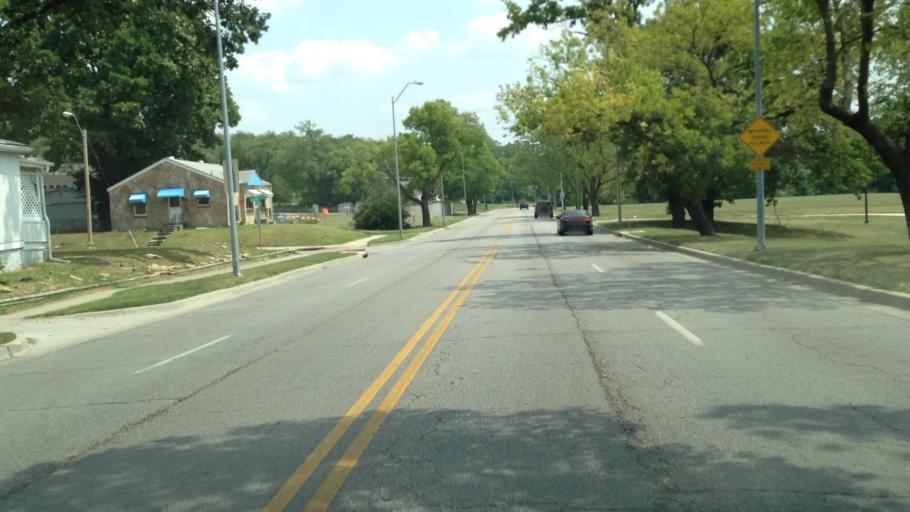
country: US
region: Missouri
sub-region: Jackson County
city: Kansas City
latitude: 39.0408
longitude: -94.5508
